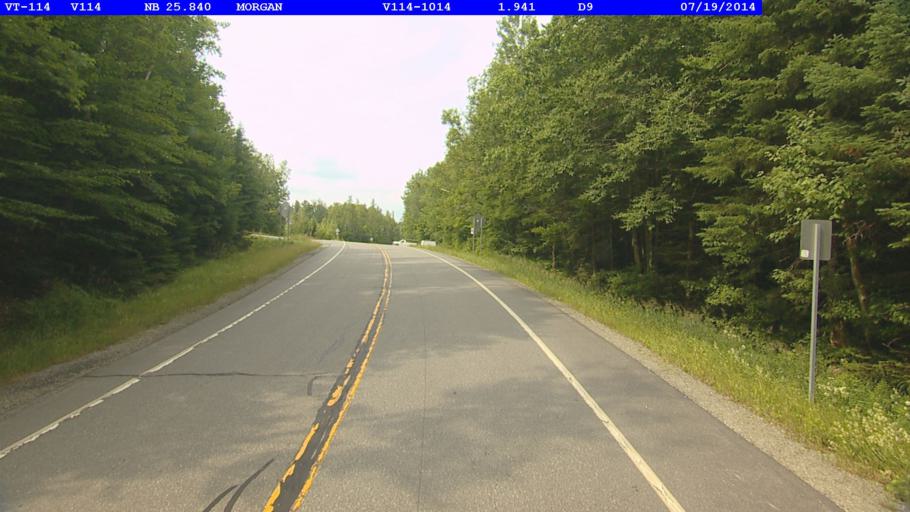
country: CA
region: Quebec
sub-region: Estrie
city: Coaticook
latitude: 44.8721
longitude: -71.9004
